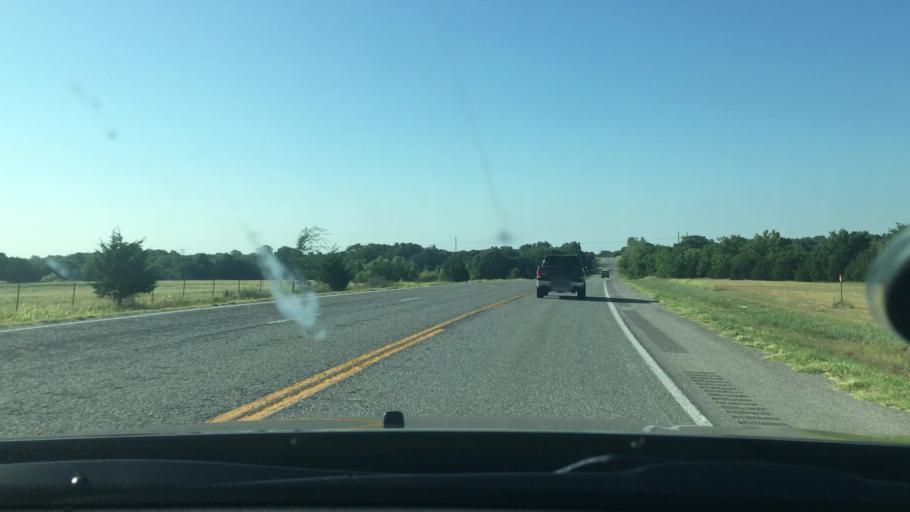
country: US
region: Oklahoma
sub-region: Johnston County
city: Tishomingo
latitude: 34.2728
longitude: -96.7753
